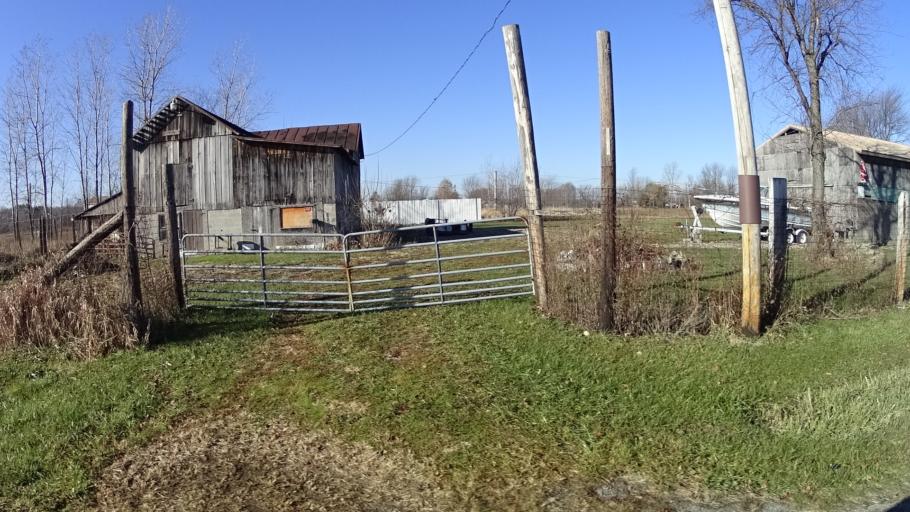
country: US
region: Ohio
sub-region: Lorain County
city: Wellington
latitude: 41.0996
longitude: -82.1808
